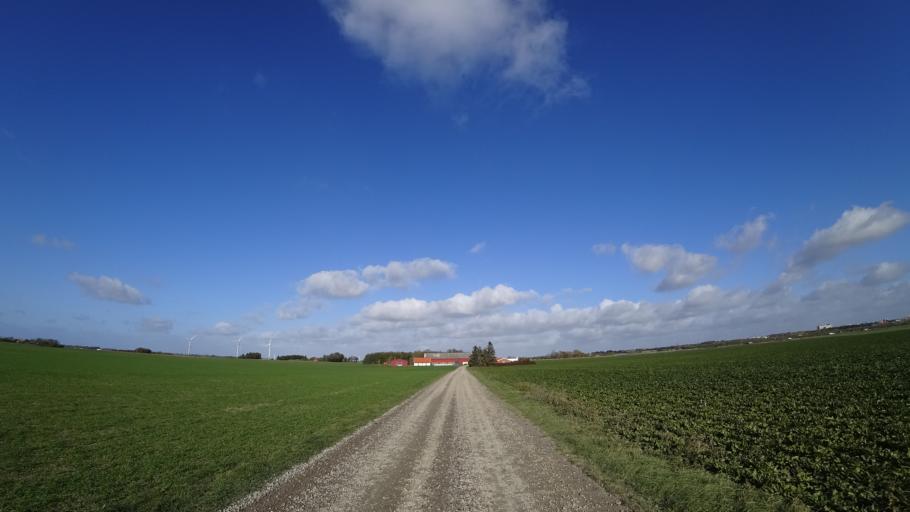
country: SE
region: Skane
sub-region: Staffanstorps Kommun
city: Hjaerup
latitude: 55.6867
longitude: 13.1442
